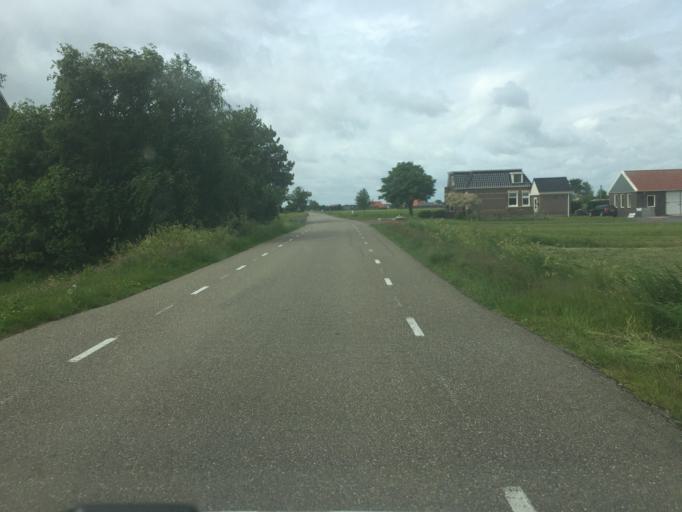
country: NL
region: Friesland
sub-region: Gemeente Lemsterland
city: Lemmer
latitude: 52.8631
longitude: 5.7479
